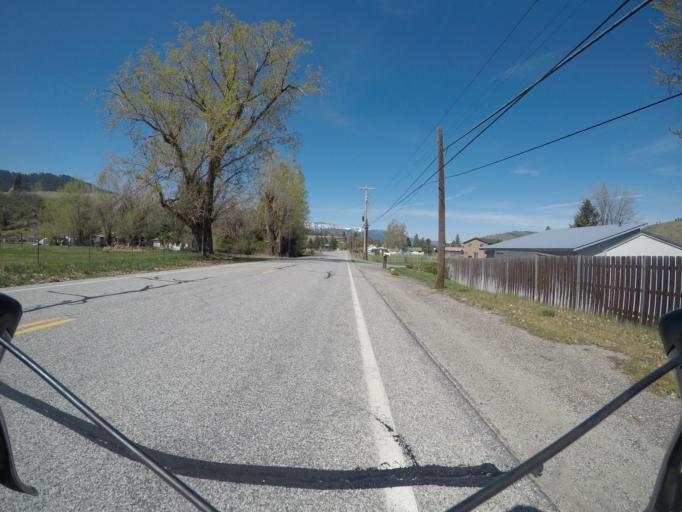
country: US
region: Washington
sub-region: Chelan County
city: Cashmere
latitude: 47.5293
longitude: -120.5411
